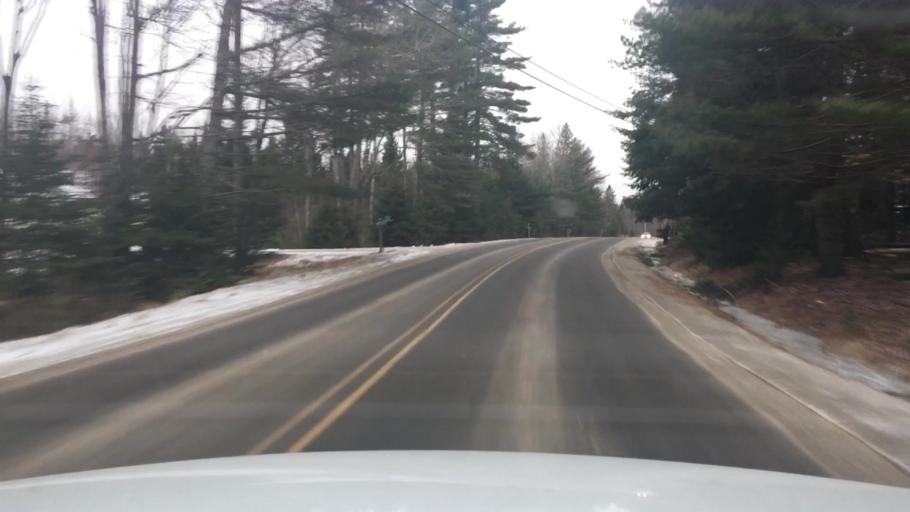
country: US
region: Maine
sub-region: Hancock County
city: Hancock
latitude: 44.5373
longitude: -68.3286
